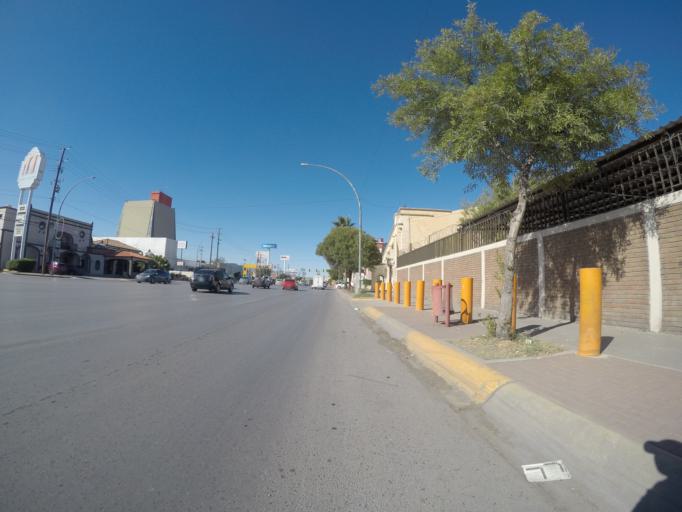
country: MX
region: Chihuahua
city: Ciudad Juarez
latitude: 31.7377
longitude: -106.4415
